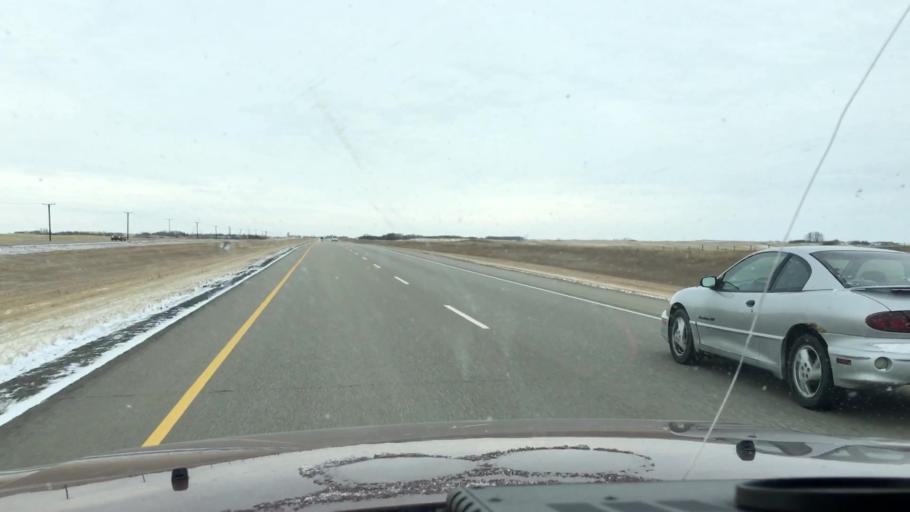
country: CA
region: Saskatchewan
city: Watrous
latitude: 51.4034
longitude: -106.1793
